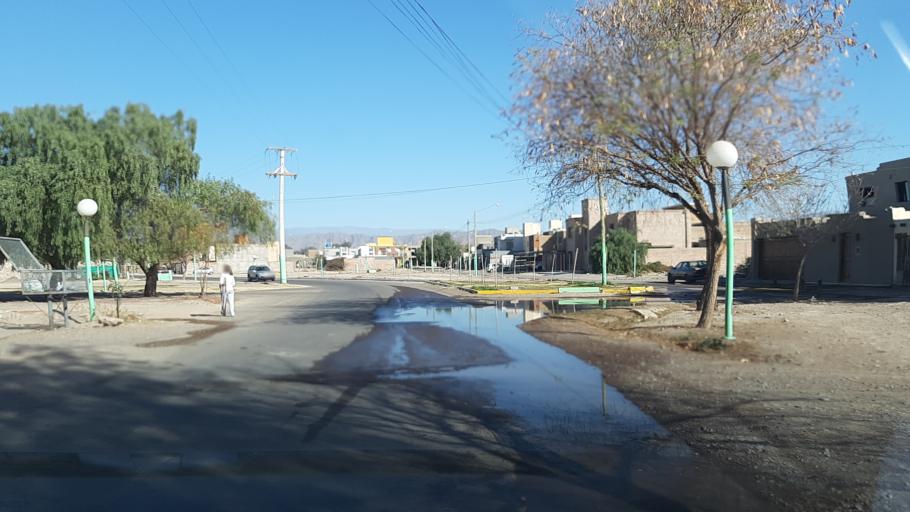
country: AR
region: San Juan
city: San Juan
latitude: -31.5198
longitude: -68.5886
